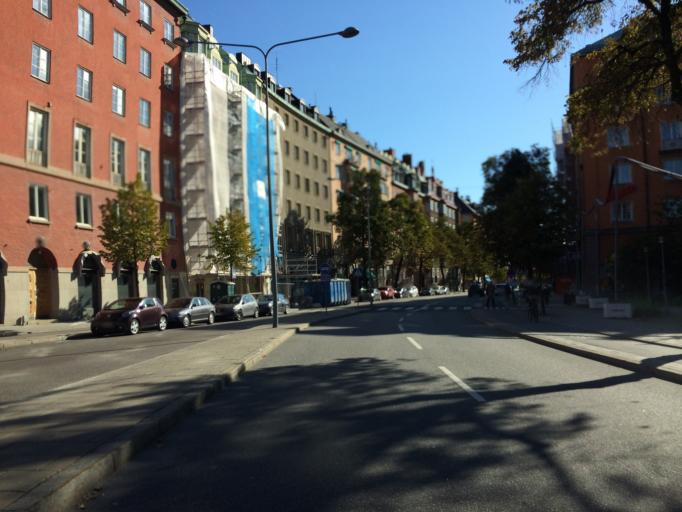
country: SE
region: Stockholm
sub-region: Stockholms Kommun
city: Stockholm
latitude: 59.3406
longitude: 18.0660
